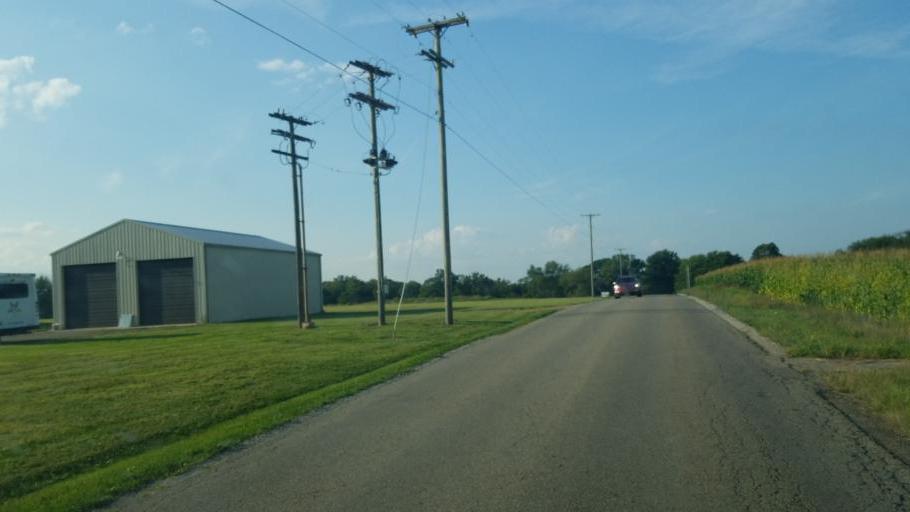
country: US
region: Ohio
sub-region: Knox County
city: Mount Vernon
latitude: 40.3884
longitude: -82.4453
